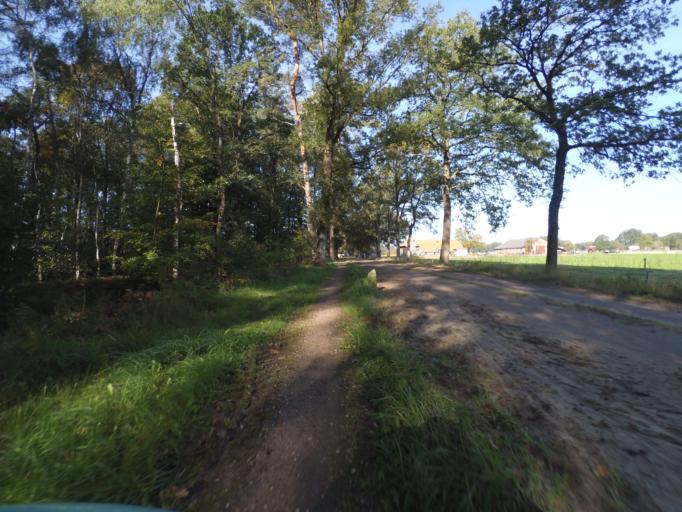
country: NL
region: Gelderland
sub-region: Gemeente Lochem
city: Barchem
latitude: 52.1084
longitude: 6.4154
